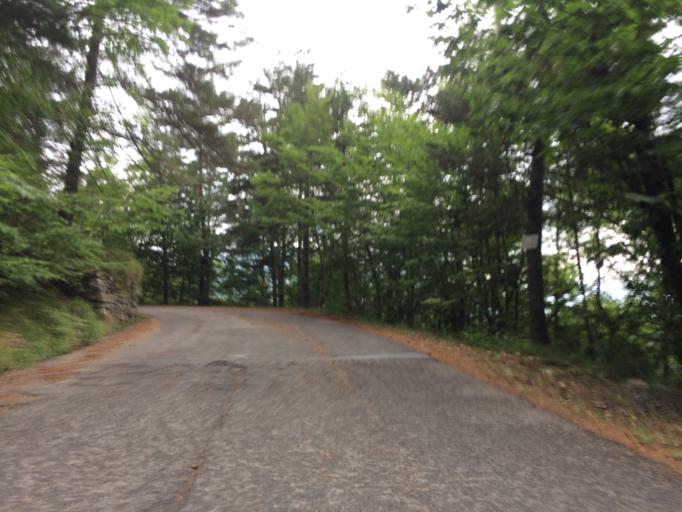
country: IT
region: Liguria
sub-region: Provincia di Imperia
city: Triora
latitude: 43.9754
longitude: 7.7449
